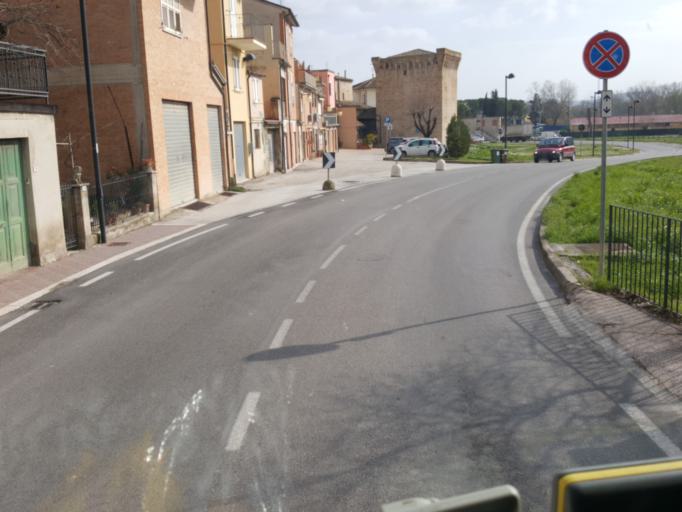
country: IT
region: The Marches
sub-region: Provincia di Macerata
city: Passo di Treia
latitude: 43.2828
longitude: 13.3283
